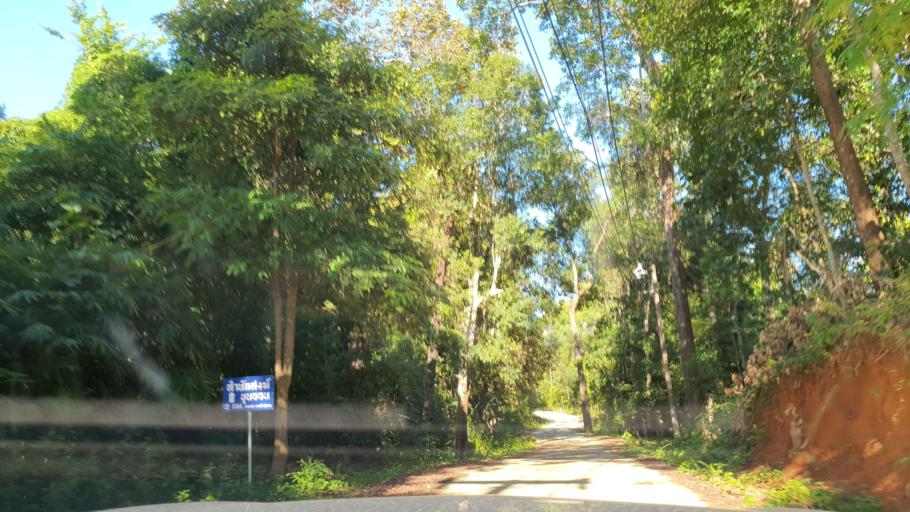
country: TH
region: Chiang Mai
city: Mae On
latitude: 18.8132
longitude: 99.3184
